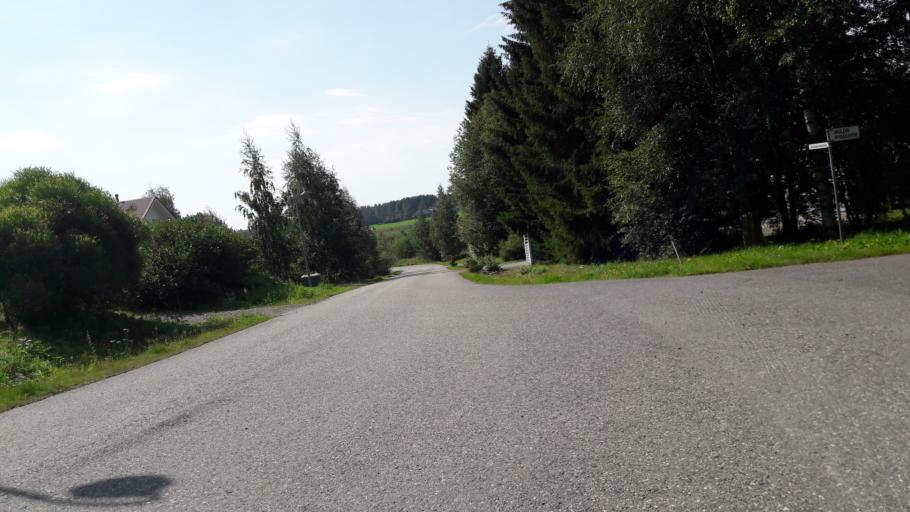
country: FI
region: North Karelia
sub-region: Joensuu
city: Joensuu
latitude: 62.5282
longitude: 29.8375
